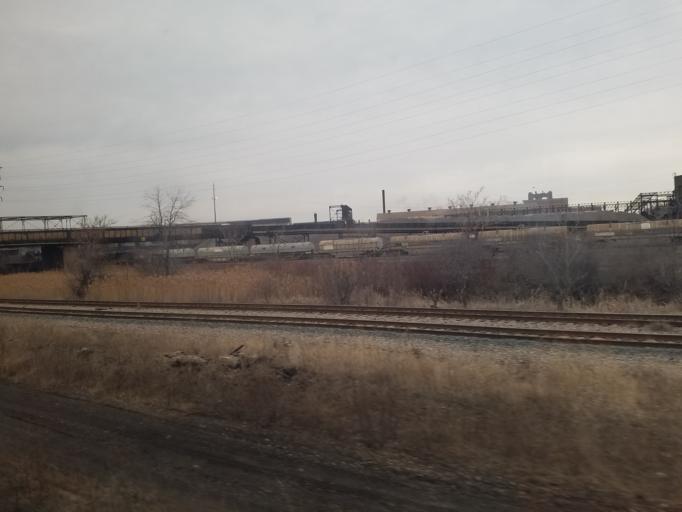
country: US
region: Indiana
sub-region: Lake County
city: East Chicago
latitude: 41.6629
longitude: -87.4564
